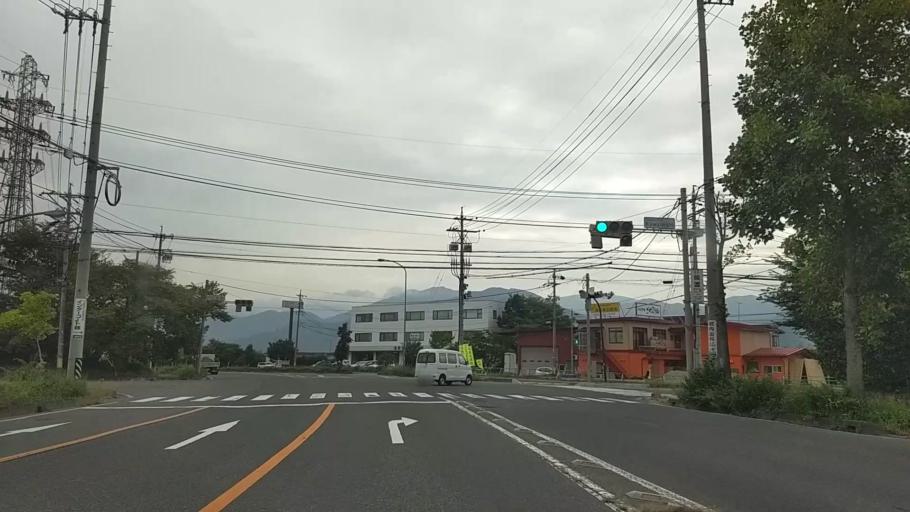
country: JP
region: Nagano
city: Nagano-shi
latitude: 36.6125
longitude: 138.2086
